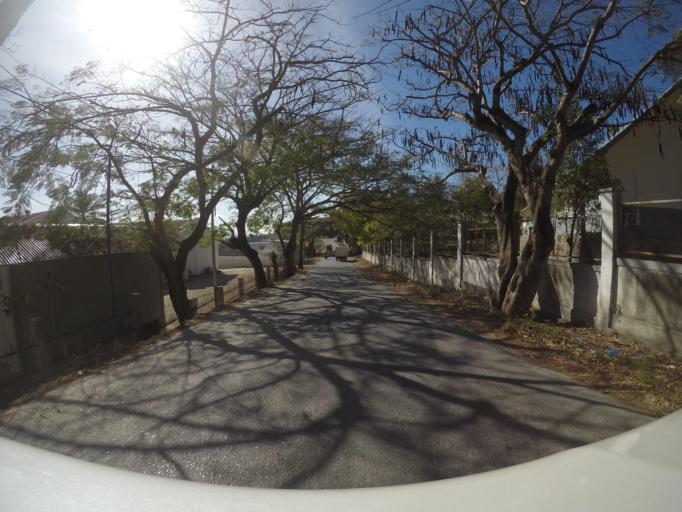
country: TL
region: Baucau
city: Baucau
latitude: -8.4627
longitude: 126.4596
